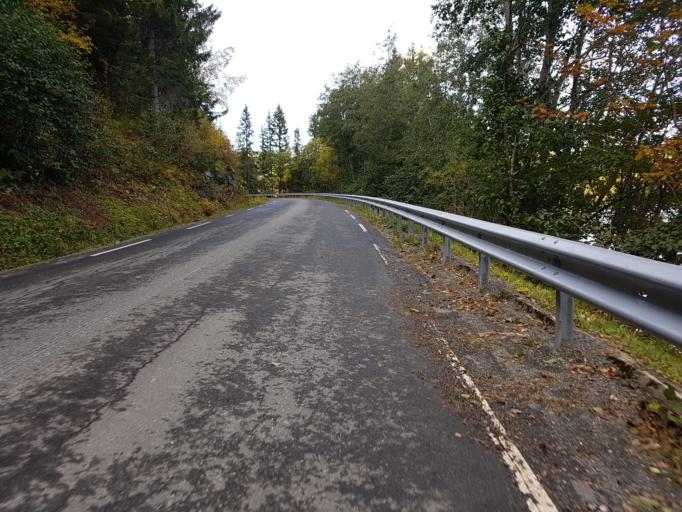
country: NO
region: Sor-Trondelag
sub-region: Klaebu
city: Klaebu
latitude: 63.3429
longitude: 10.5536
